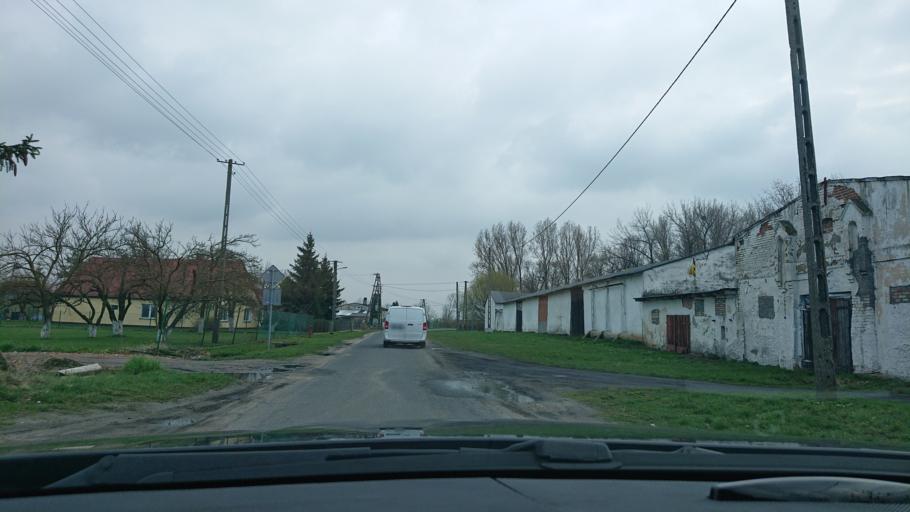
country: PL
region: Greater Poland Voivodeship
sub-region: Powiat gnieznienski
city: Lubowo
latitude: 52.5480
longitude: 17.4956
